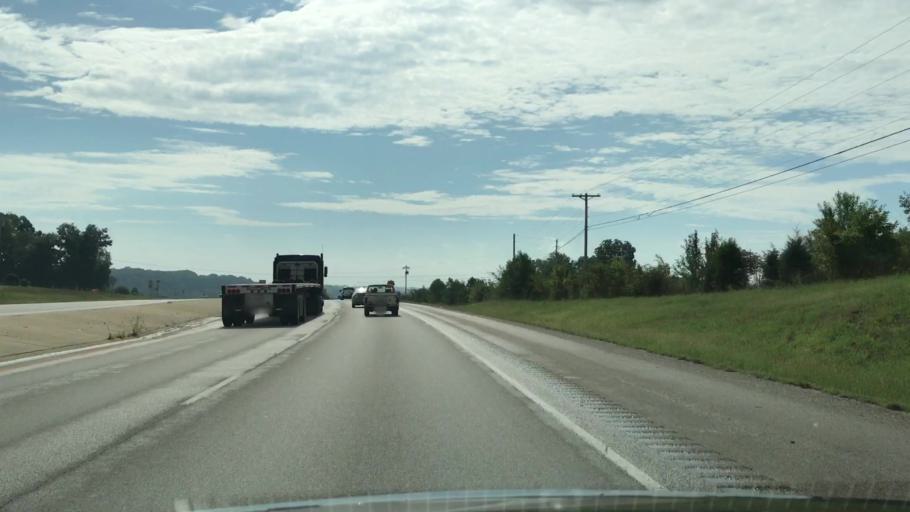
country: US
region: Kentucky
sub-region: Warren County
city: Plano
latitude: 36.9032
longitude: -86.3970
